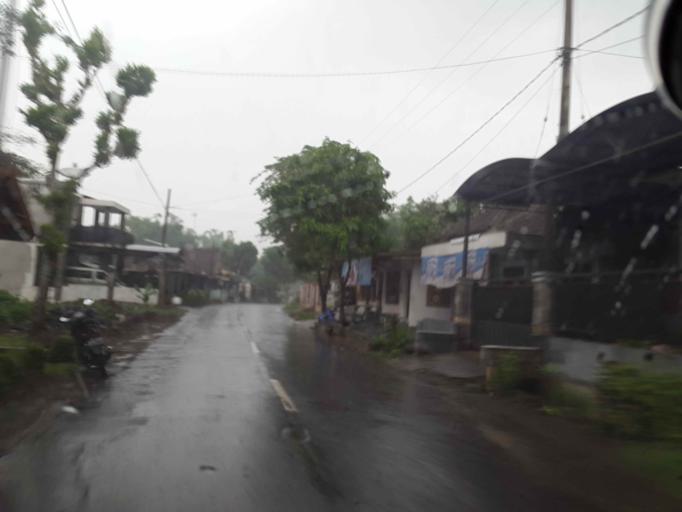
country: ID
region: East Java
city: Kedungkrajan
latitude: -8.1478
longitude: 112.5823
